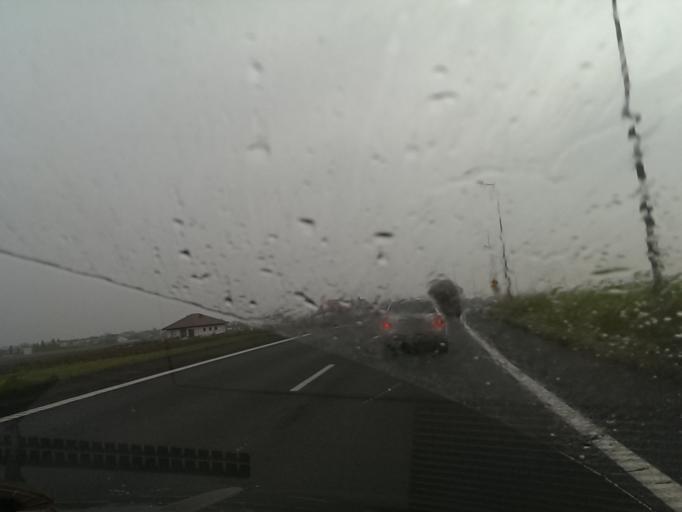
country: PL
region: Kujawsko-Pomorskie
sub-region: Powiat nakielski
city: Naklo nad Notecia
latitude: 53.1521
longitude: 17.6128
